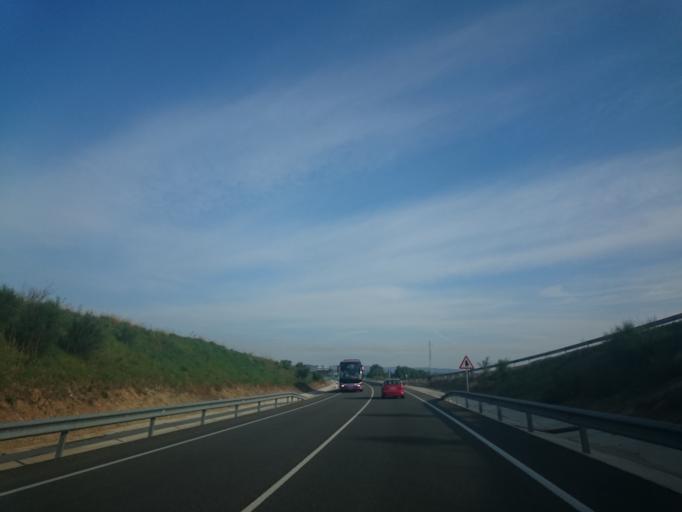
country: ES
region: Catalonia
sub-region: Provincia de Barcelona
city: el Pla del Penedes
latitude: 41.4044
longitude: 1.7036
